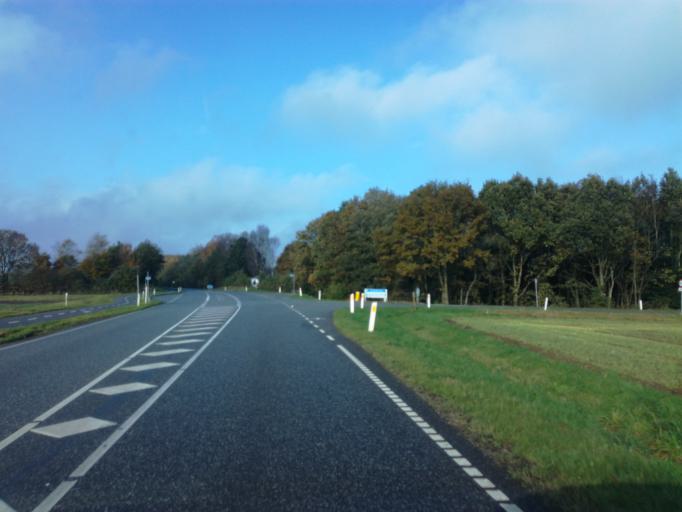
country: DK
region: South Denmark
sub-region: Vejle Kommune
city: Borkop
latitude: 55.6740
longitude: 9.6129
